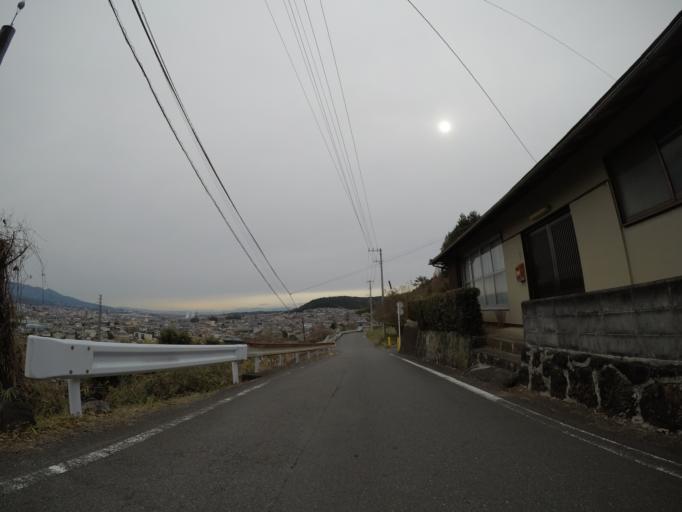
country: JP
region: Shizuoka
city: Fujinomiya
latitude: 35.2290
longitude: 138.5899
